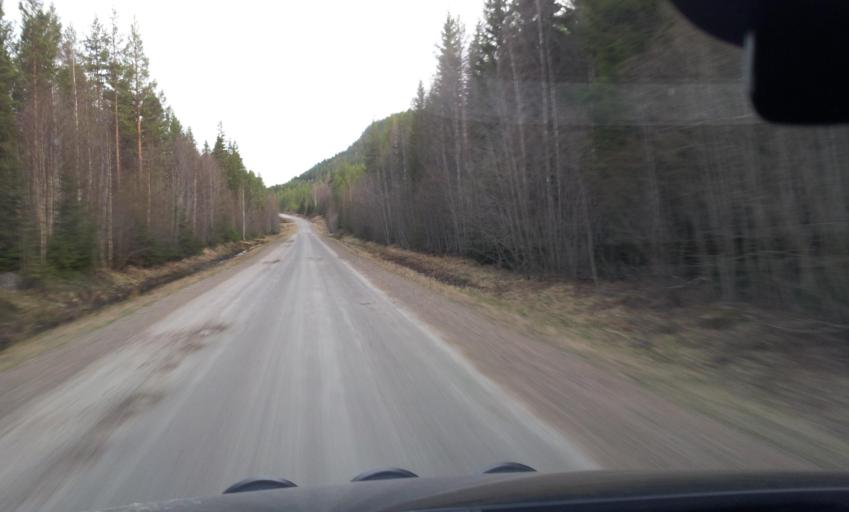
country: SE
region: Gaevleborg
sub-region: Ljusdals Kommun
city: Farila
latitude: 62.0367
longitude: 15.8216
